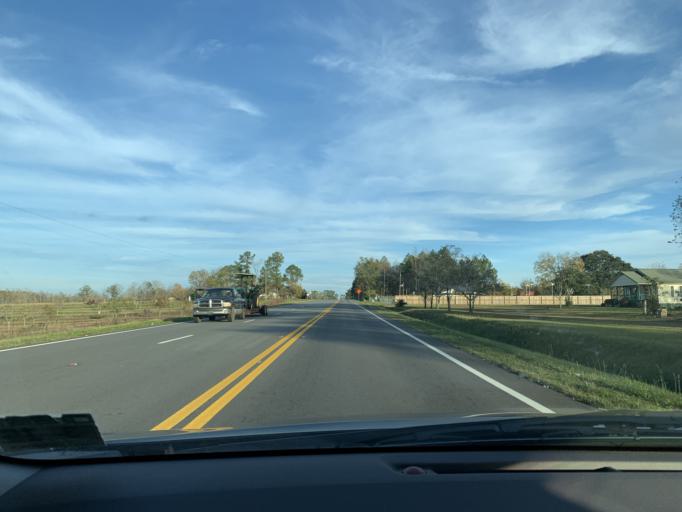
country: US
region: Georgia
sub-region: Irwin County
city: Ocilla
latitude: 31.5958
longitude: -83.1584
